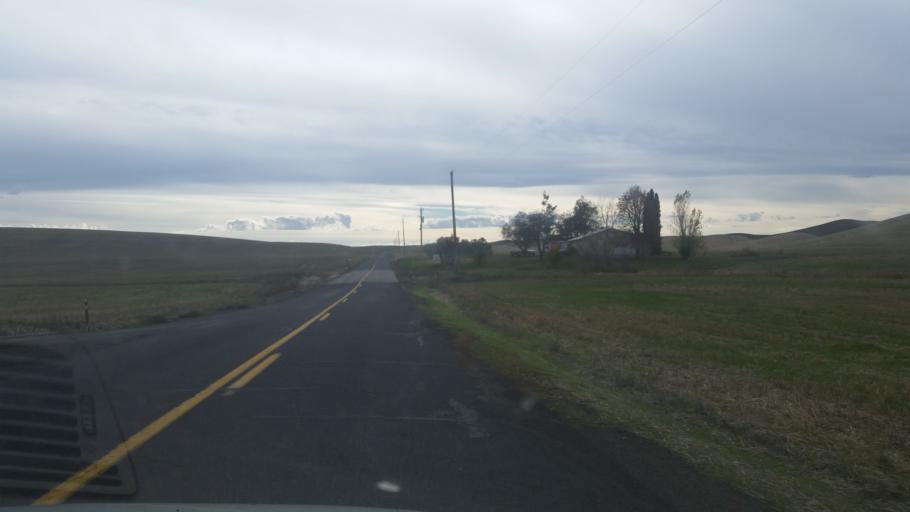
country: US
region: Washington
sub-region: Spokane County
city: Cheney
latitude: 47.3035
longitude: -117.4924
